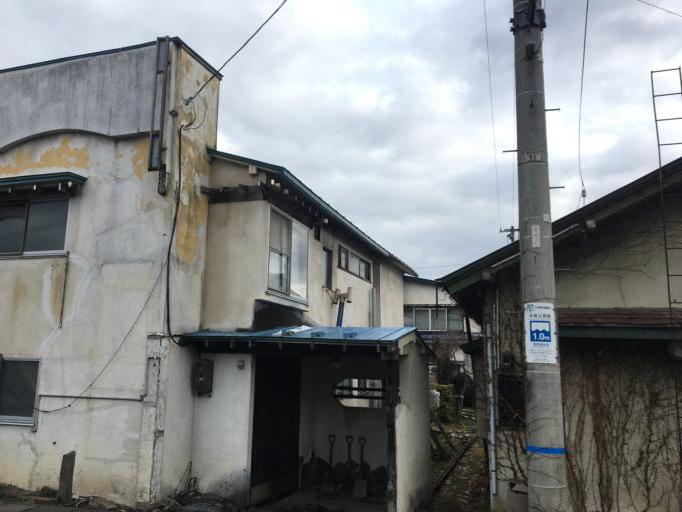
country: JP
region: Aomori
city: Hirosaki
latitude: 40.5216
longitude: 140.5638
